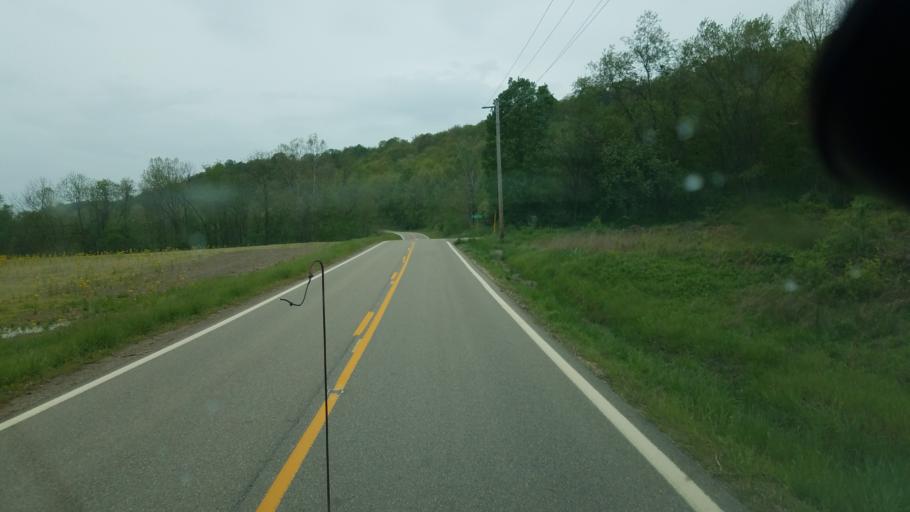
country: US
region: Ohio
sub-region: Guernsey County
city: Mantua
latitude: 40.1615
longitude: -81.6322
